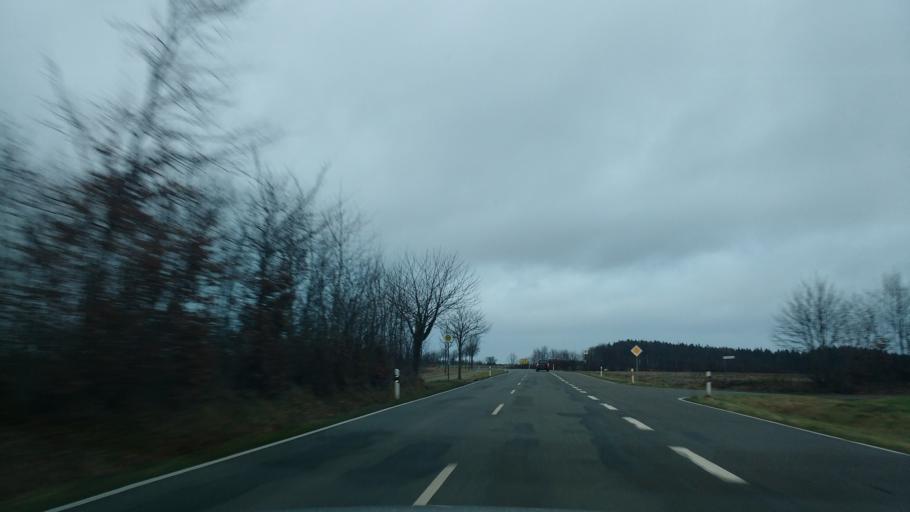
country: DE
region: Schleswig-Holstein
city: Nindorf
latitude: 54.1239
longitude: 9.7051
